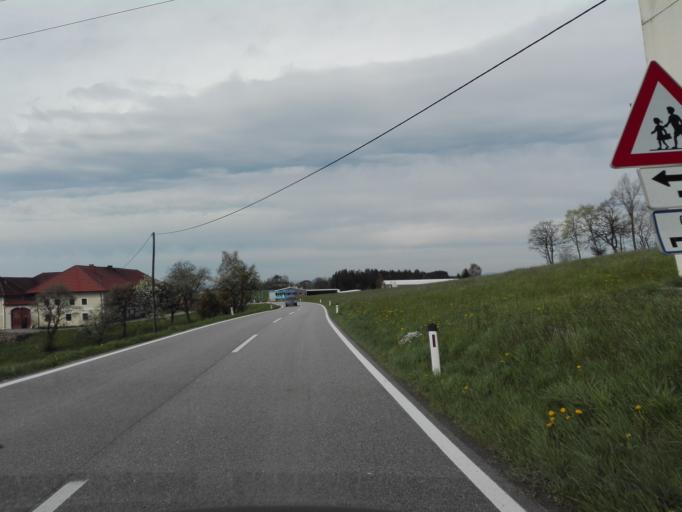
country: AT
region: Upper Austria
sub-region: Politischer Bezirk Urfahr-Umgebung
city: Eidenberg
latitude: 48.3713
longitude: 14.2181
